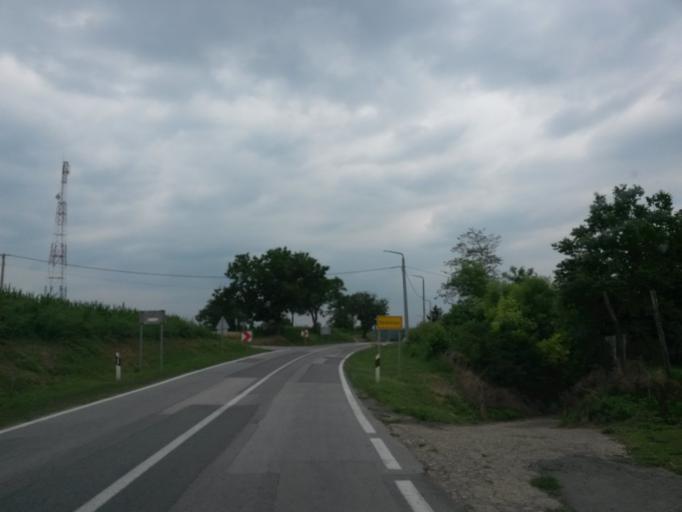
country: HR
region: Vukovarsko-Srijemska
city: Lovas
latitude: 45.2625
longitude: 19.1650
